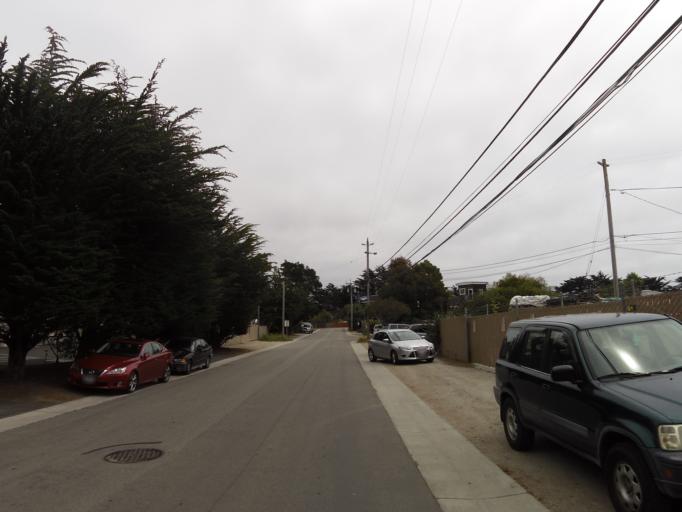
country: US
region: California
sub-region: San Mateo County
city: El Granada
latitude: 37.5056
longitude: -122.4895
